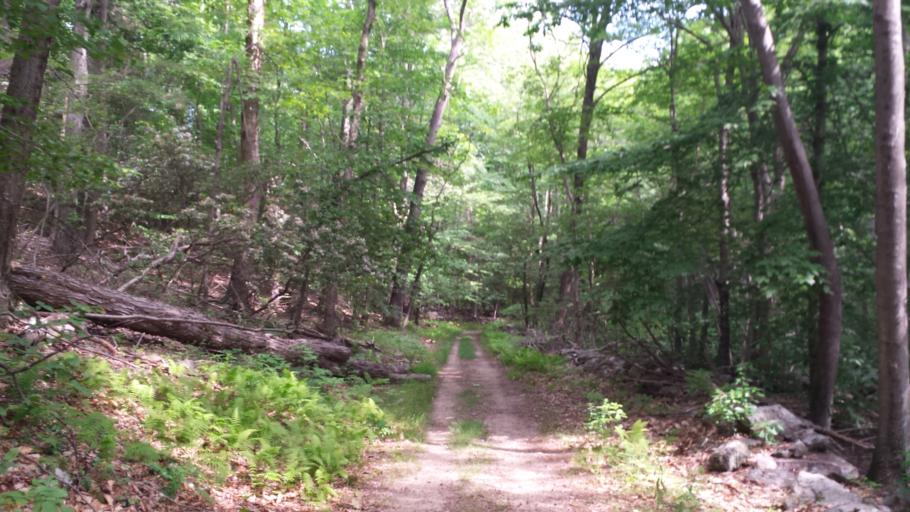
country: US
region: New York
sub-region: Westchester County
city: Pound Ridge
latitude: 41.2379
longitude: -73.5877
